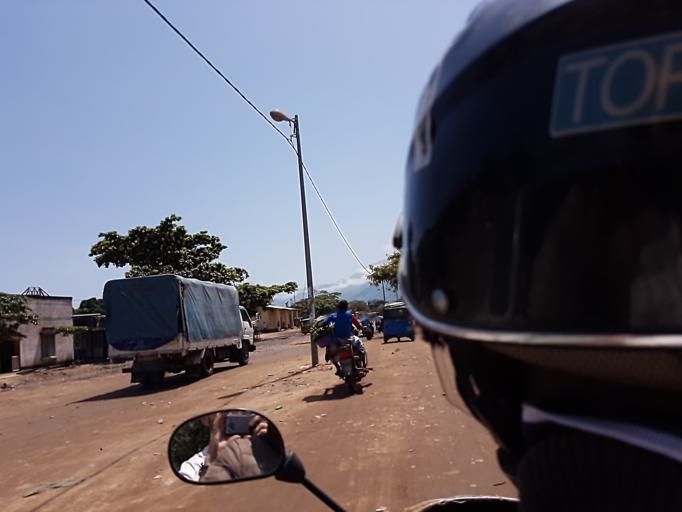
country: CD
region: South Kivu
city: Uvira
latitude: -3.3659
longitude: 29.1486
